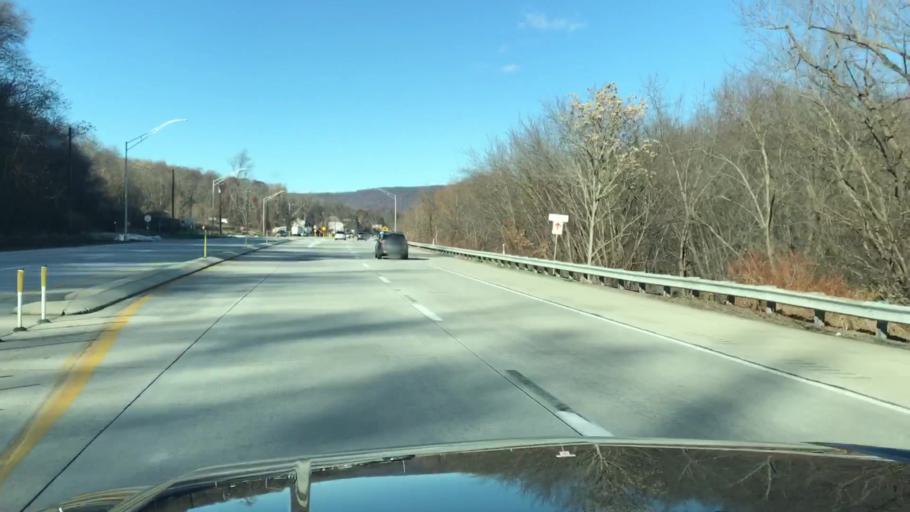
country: US
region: Pennsylvania
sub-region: Dauphin County
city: Millersburg
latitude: 40.4937
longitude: -76.9627
